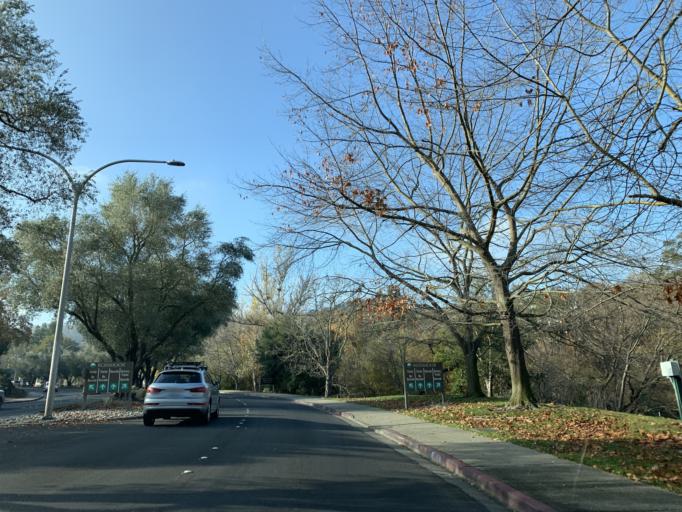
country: US
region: California
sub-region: Contra Costa County
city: Saranap
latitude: 37.8746
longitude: -122.0738
